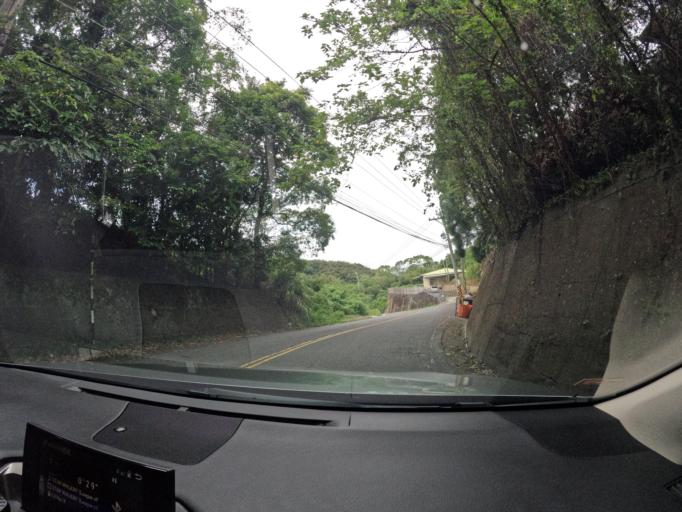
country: TW
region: Taiwan
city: Fengyuan
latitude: 24.3220
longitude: 120.8799
